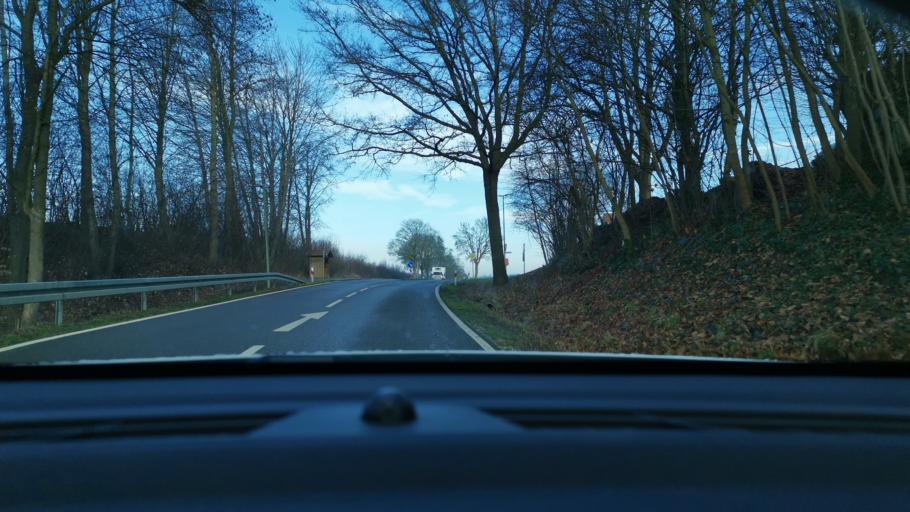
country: DE
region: Bavaria
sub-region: Swabia
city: Petersdorf
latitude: 48.5185
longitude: 11.0338
